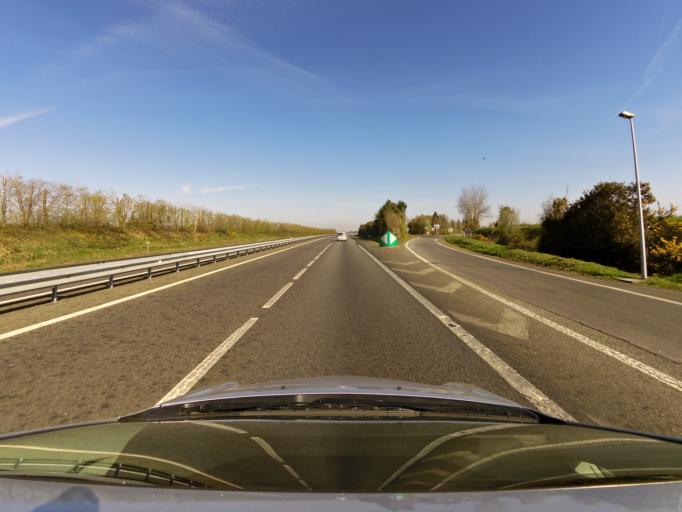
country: FR
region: Brittany
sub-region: Departement d'Ille-et-Vilaine
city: Plelan-le-Grand
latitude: 47.9709
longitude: -2.0965
